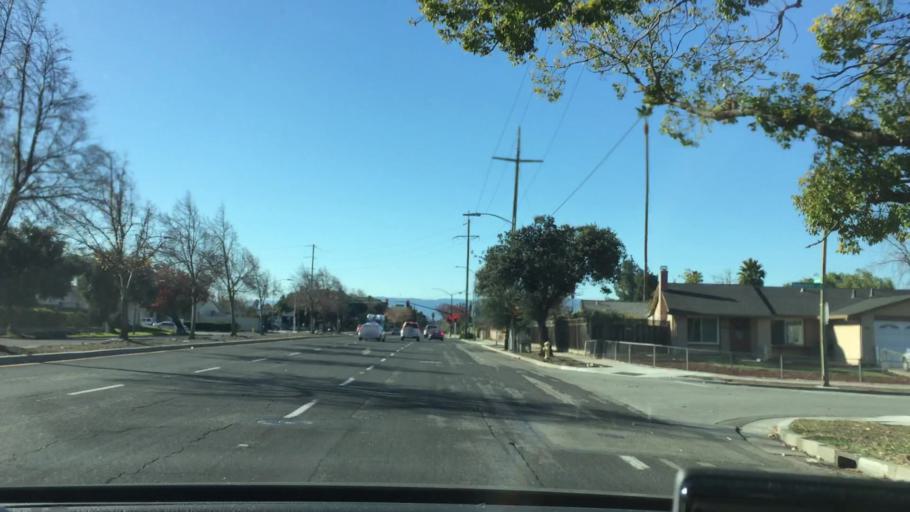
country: US
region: California
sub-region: Santa Clara County
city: Milpitas
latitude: 37.3924
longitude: -121.8780
